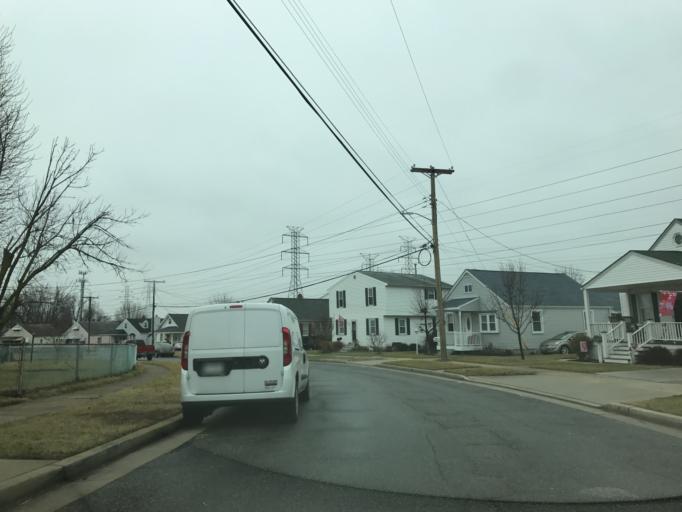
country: US
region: Maryland
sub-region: Baltimore County
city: Essex
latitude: 39.2845
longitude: -76.5033
